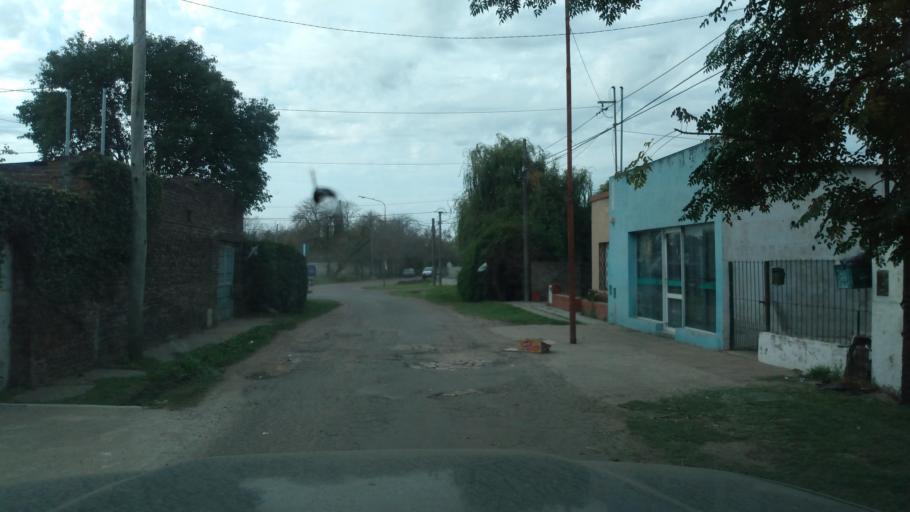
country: AR
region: Buenos Aires
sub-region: Partido de Lujan
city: Lujan
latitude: -34.6021
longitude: -59.1755
